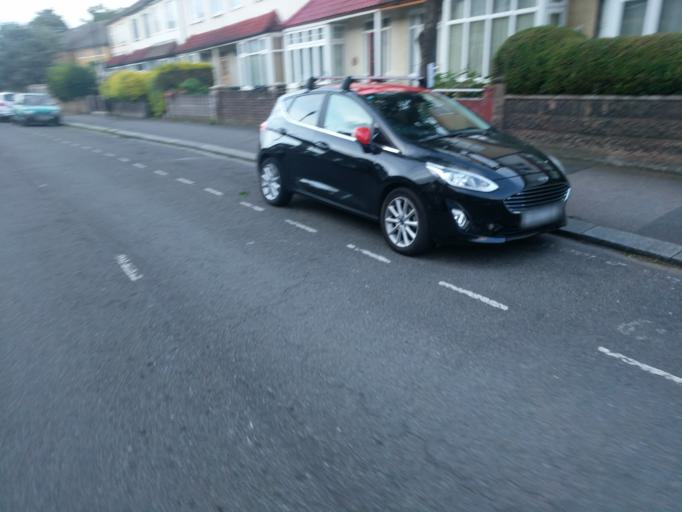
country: GB
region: England
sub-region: Greater London
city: Catford
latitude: 51.4552
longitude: -0.0207
